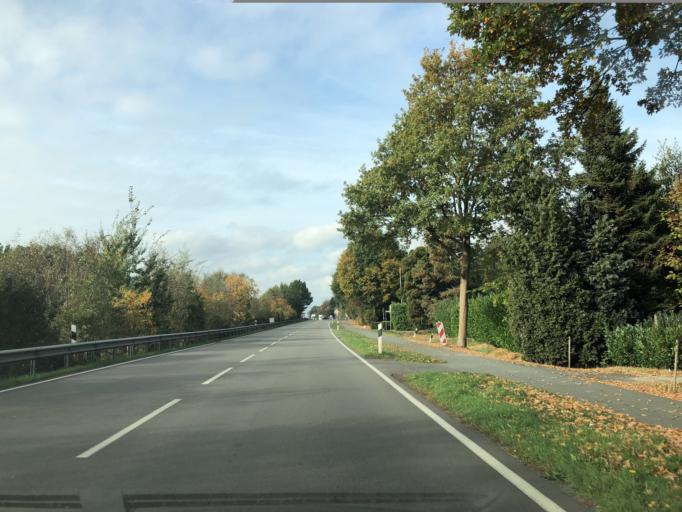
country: DE
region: Lower Saxony
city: Edewecht
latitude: 53.0868
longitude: 7.9447
